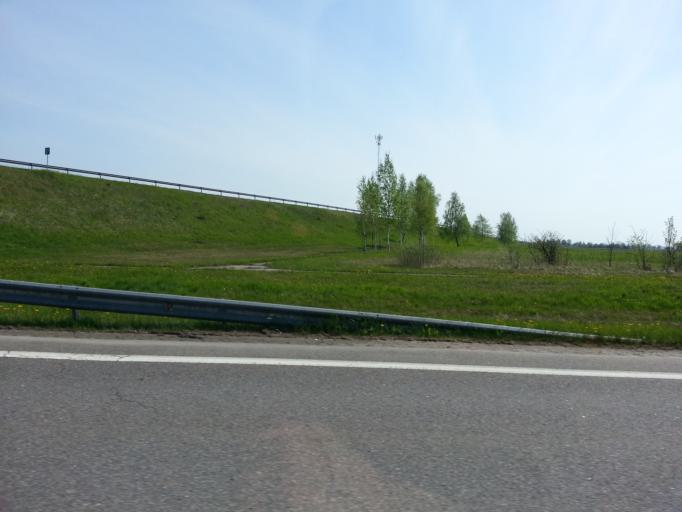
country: LT
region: Vilnius County
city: Ukmerge
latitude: 55.3968
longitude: 24.7016
